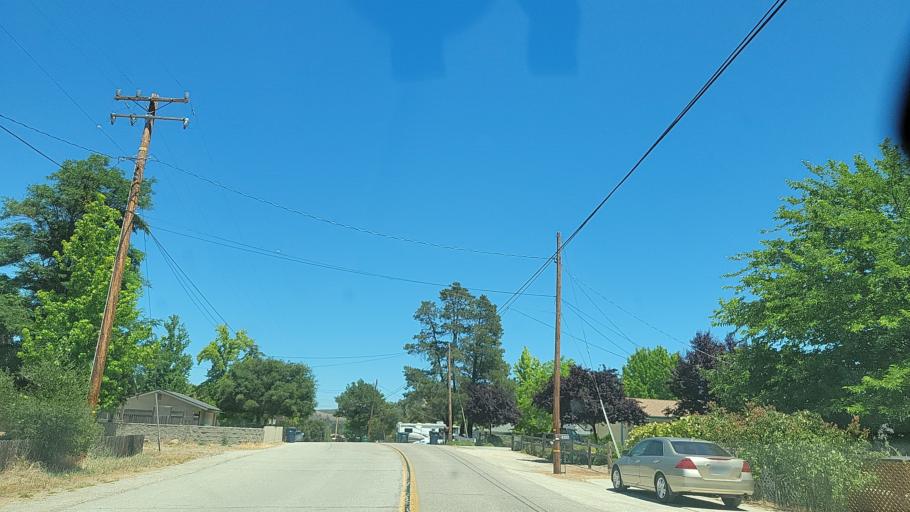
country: US
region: California
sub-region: San Luis Obispo County
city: Atascadero
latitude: 35.4673
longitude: -120.6583
